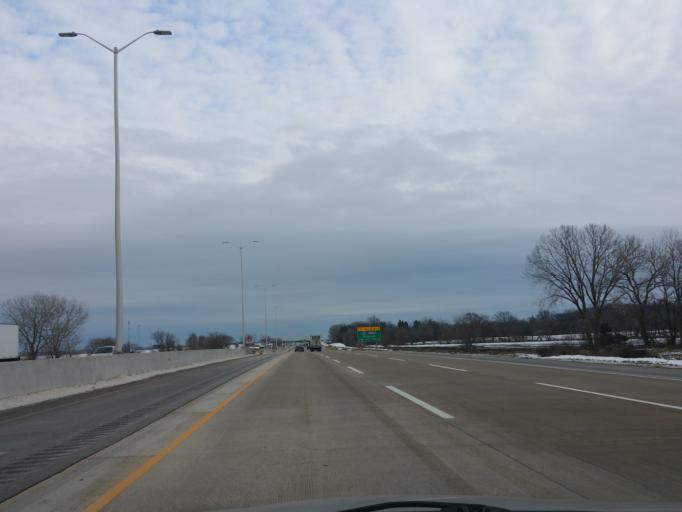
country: US
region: Illinois
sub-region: McHenry County
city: Marengo
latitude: 42.1815
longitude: -88.6289
